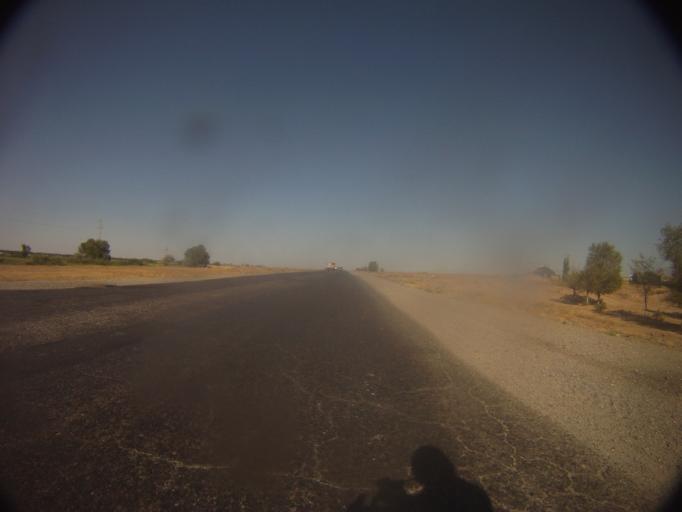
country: KZ
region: Zhambyl
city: Sarykemer
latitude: 42.9259
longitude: 71.4865
